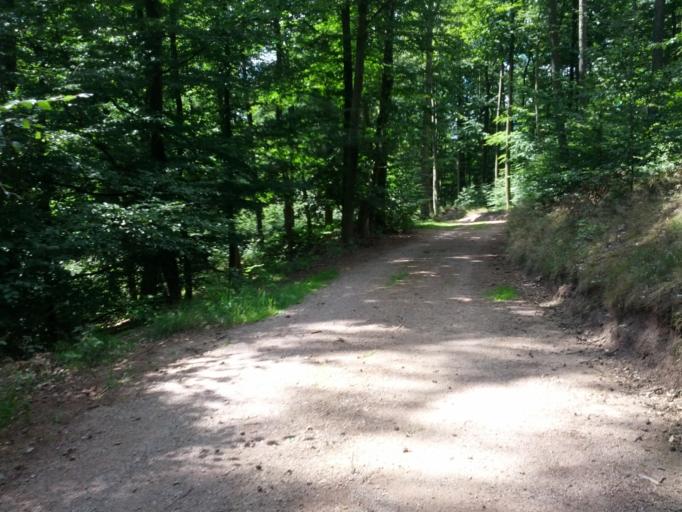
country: DE
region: Thuringia
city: Wolfsburg-Unkeroda
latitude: 50.9448
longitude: 10.2917
